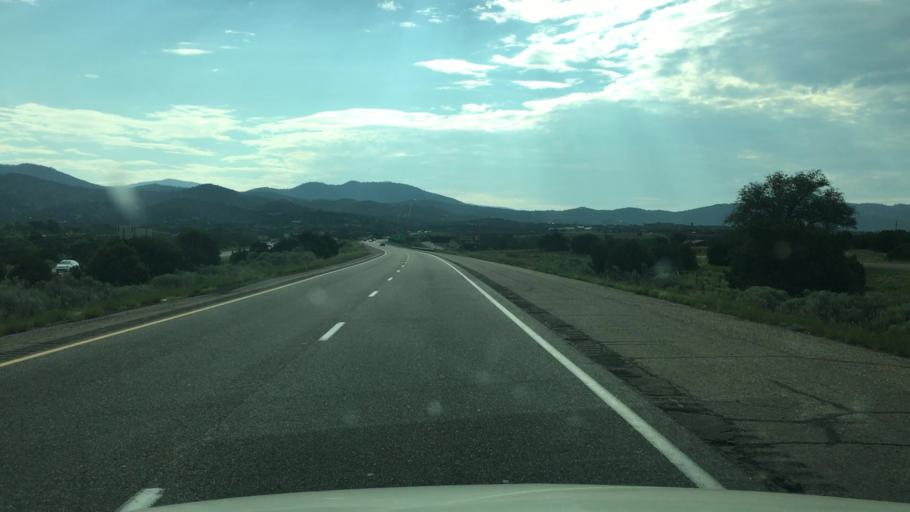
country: US
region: New Mexico
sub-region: Santa Fe County
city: Santa Fe
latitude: 35.6370
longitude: -105.9447
